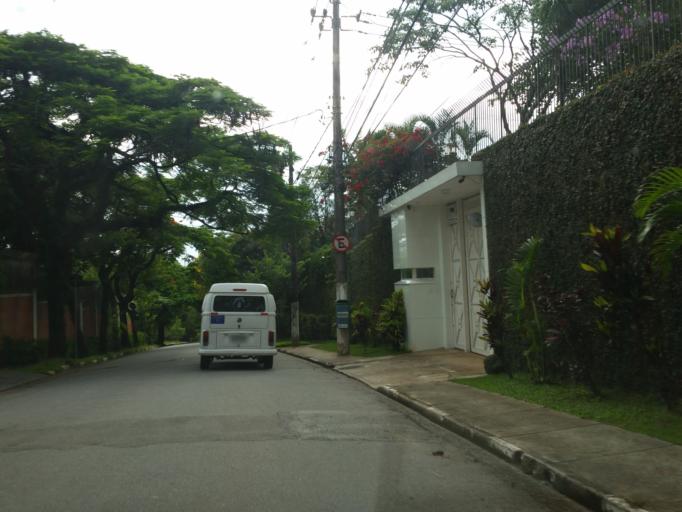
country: BR
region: Sao Paulo
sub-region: Diadema
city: Diadema
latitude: -23.6403
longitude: -46.6808
